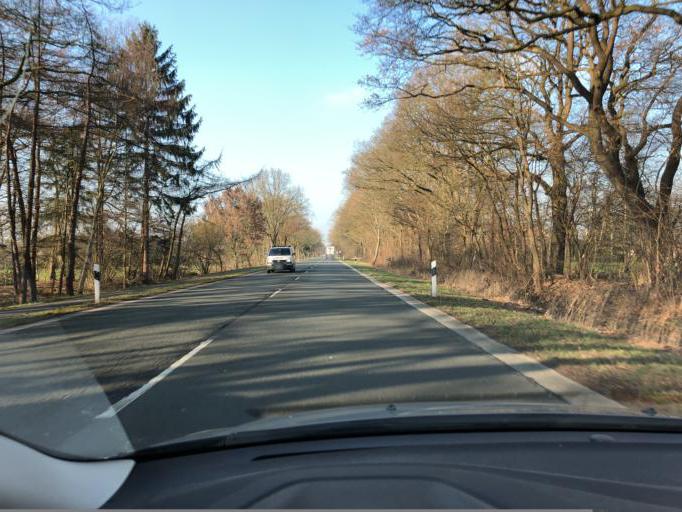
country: DE
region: Lower Saxony
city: Westerstede
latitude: 53.2936
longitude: 7.8551
